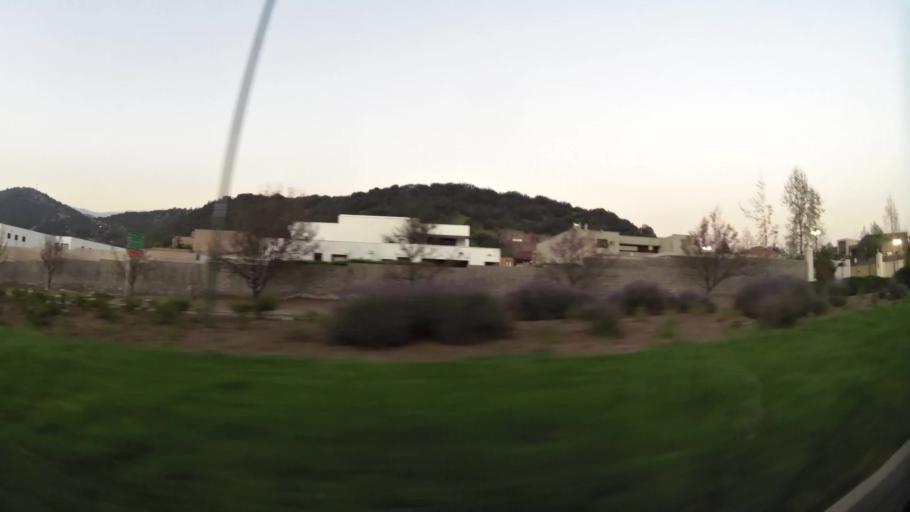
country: CL
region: Santiago Metropolitan
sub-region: Provincia de Chacabuco
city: Chicureo Abajo
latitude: -33.3211
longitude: -70.5439
